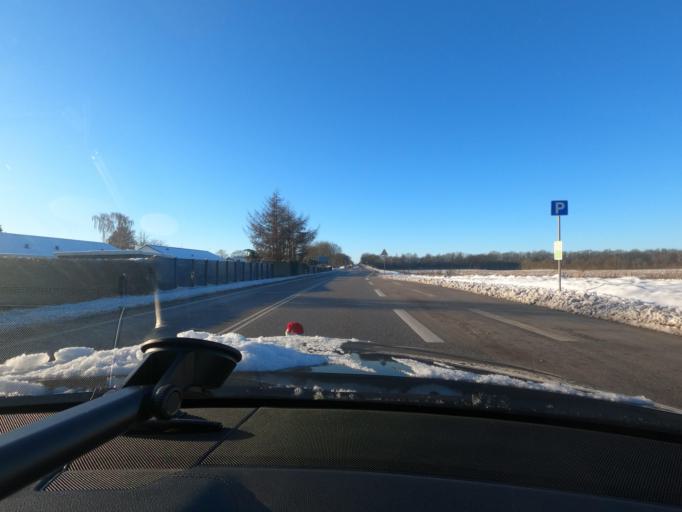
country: DK
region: South Denmark
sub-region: Aabenraa Kommune
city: Rodekro
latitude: 55.0746
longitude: 9.3392
